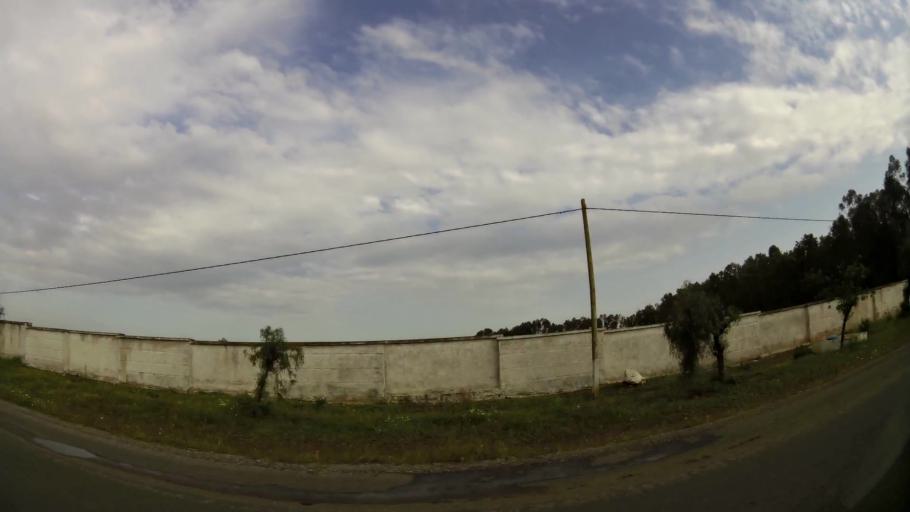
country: MA
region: Rabat-Sale-Zemmour-Zaer
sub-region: Khemisset
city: Khemisset
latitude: 33.7976
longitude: -6.0995
